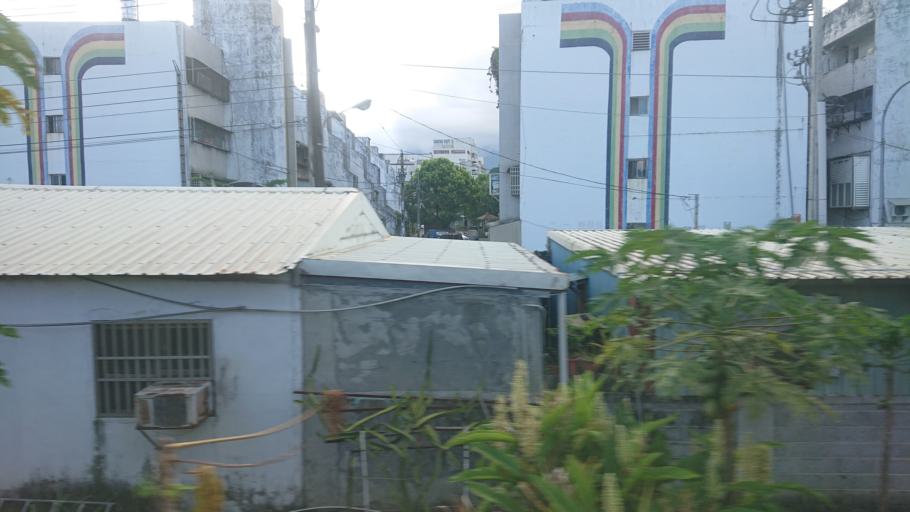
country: TW
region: Taiwan
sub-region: Hualien
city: Hualian
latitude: 23.9867
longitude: 121.5978
